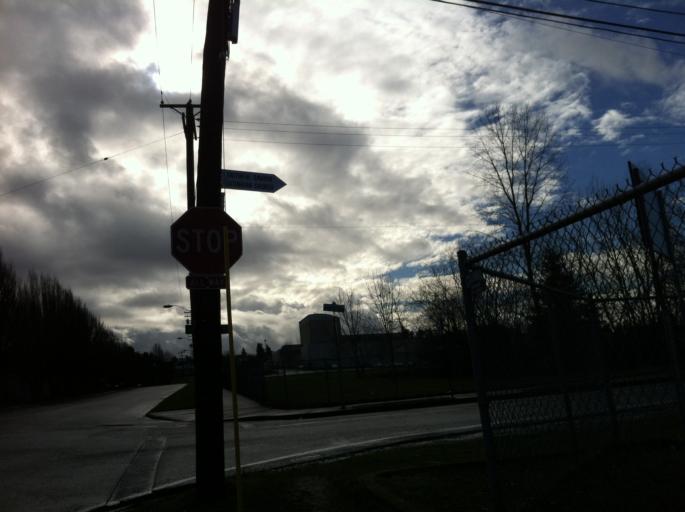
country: US
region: Oregon
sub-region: Multnomah County
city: Lents
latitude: 45.5554
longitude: -122.5383
